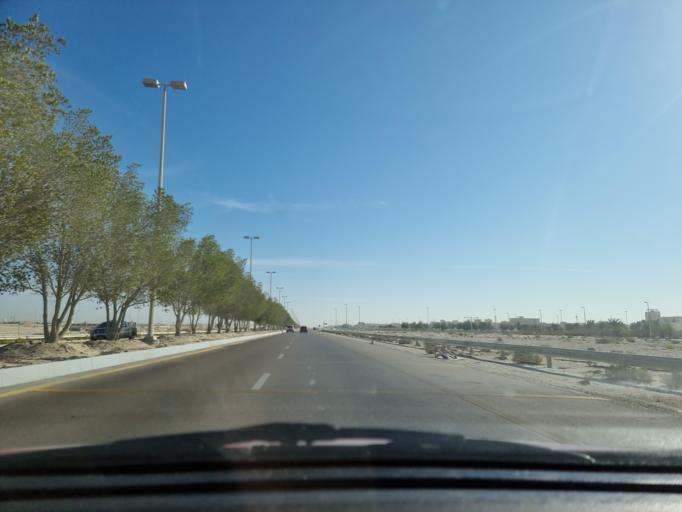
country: AE
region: Abu Dhabi
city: Abu Dhabi
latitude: 24.3987
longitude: 54.7006
